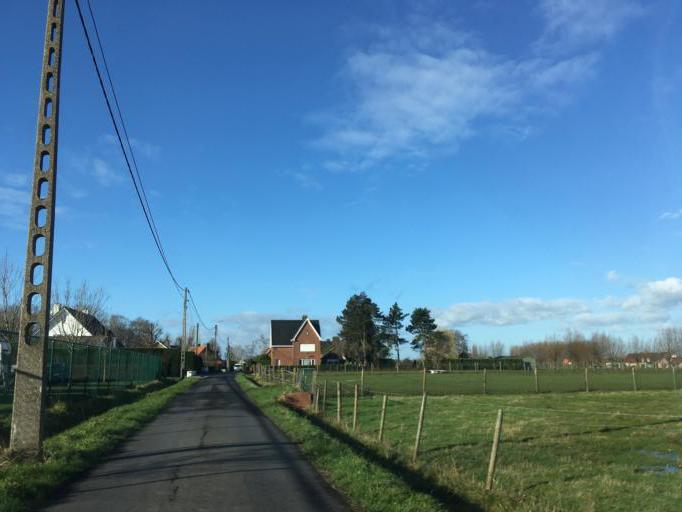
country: BE
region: Flanders
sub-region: Provincie West-Vlaanderen
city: Ardooie
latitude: 50.9633
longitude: 3.1713
